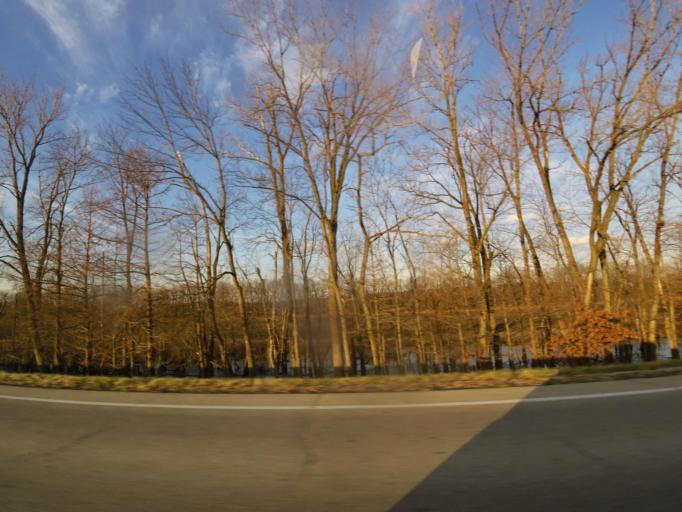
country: US
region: Illinois
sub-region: Fayette County
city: Vandalia
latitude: 38.9431
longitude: -89.0852
